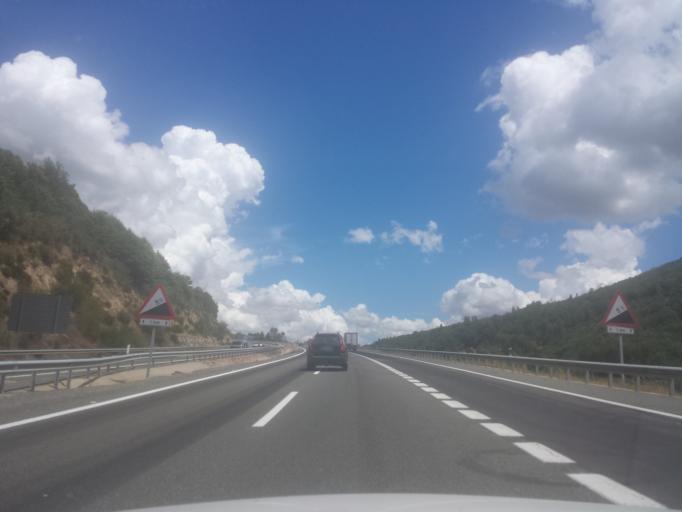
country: ES
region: Castille and Leon
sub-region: Provincia de Salamanca
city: Penacaballera
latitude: 40.3310
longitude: -5.8550
